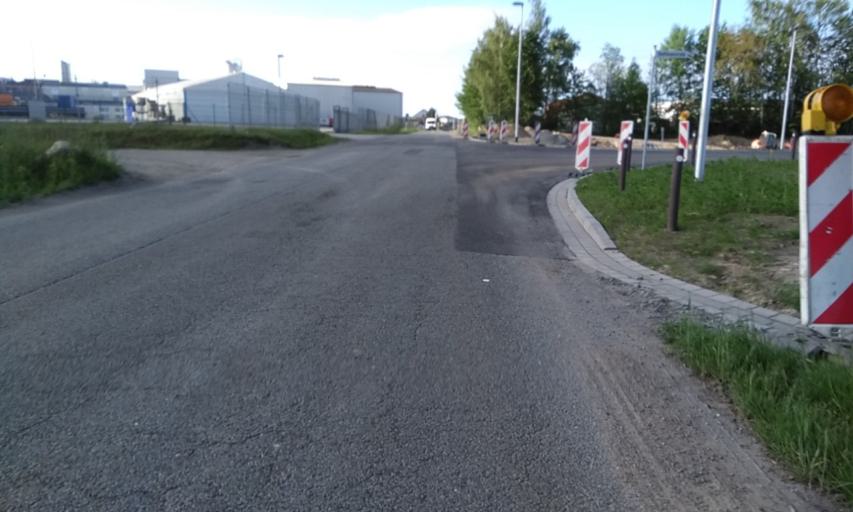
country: DE
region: Lower Saxony
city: Apensen
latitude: 53.4454
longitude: 9.6186
